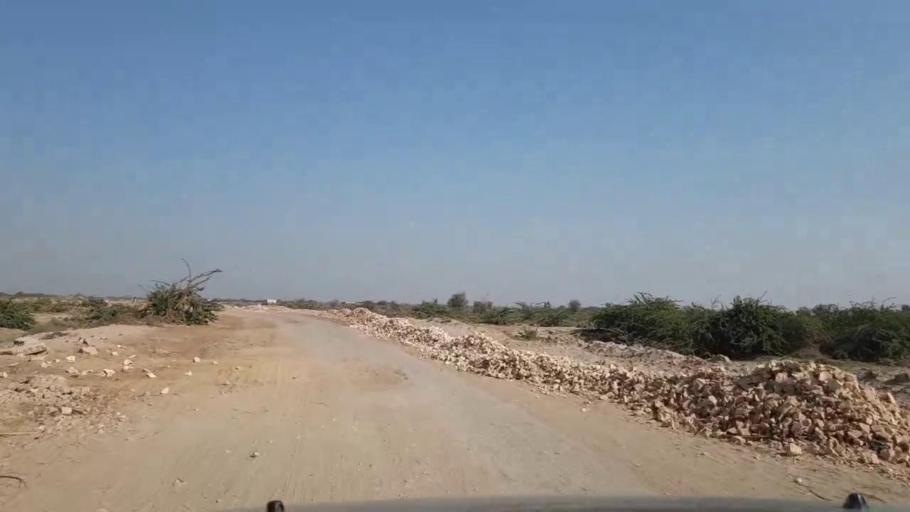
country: PK
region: Sindh
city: Digri
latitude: 24.9691
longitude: 69.1134
